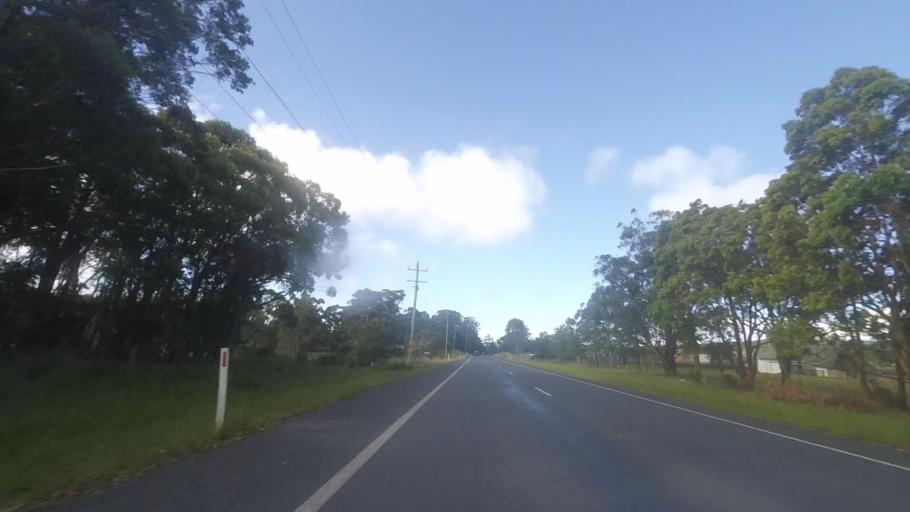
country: AU
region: New South Wales
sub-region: Great Lakes
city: Forster
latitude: -32.3598
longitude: 152.5033
